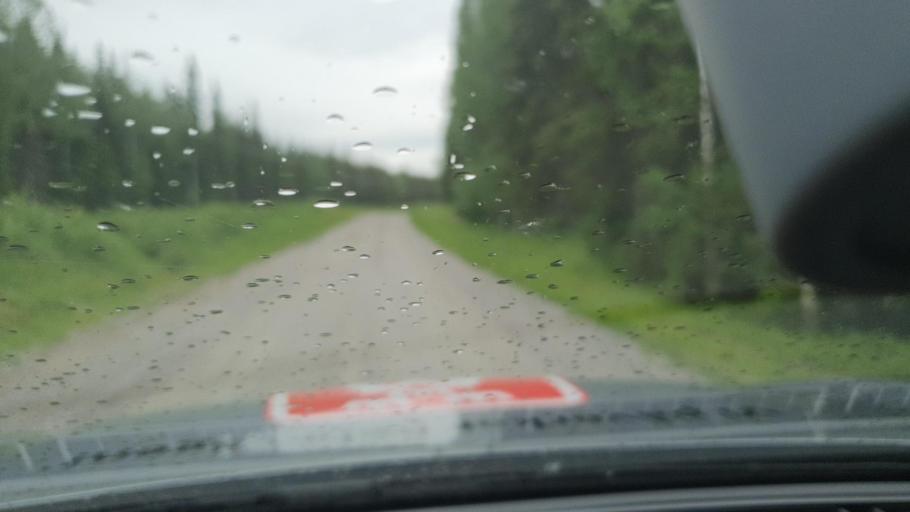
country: SE
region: Norrbotten
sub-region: Kalix Kommun
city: Rolfs
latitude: 66.0597
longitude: 23.0244
